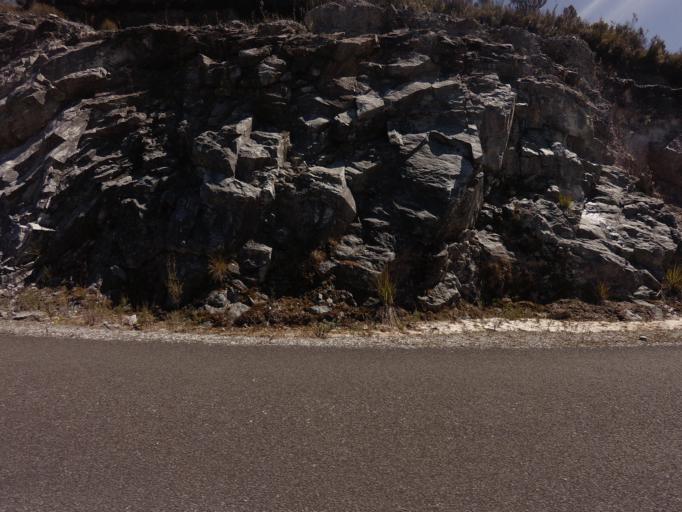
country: AU
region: Tasmania
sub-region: West Coast
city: Queenstown
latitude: -42.7402
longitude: 145.9809
